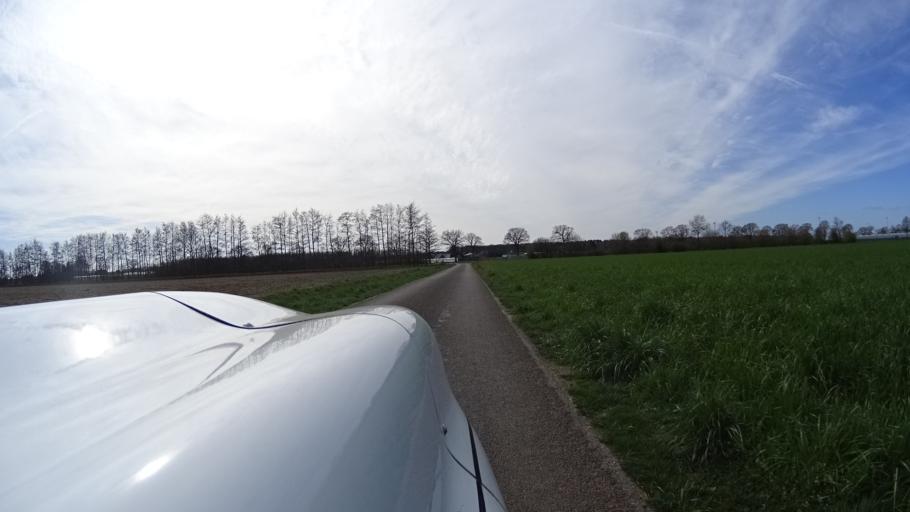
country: DE
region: North Rhine-Westphalia
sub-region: Regierungsbezirk Dusseldorf
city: Kevelaer
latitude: 51.5669
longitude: 6.2056
